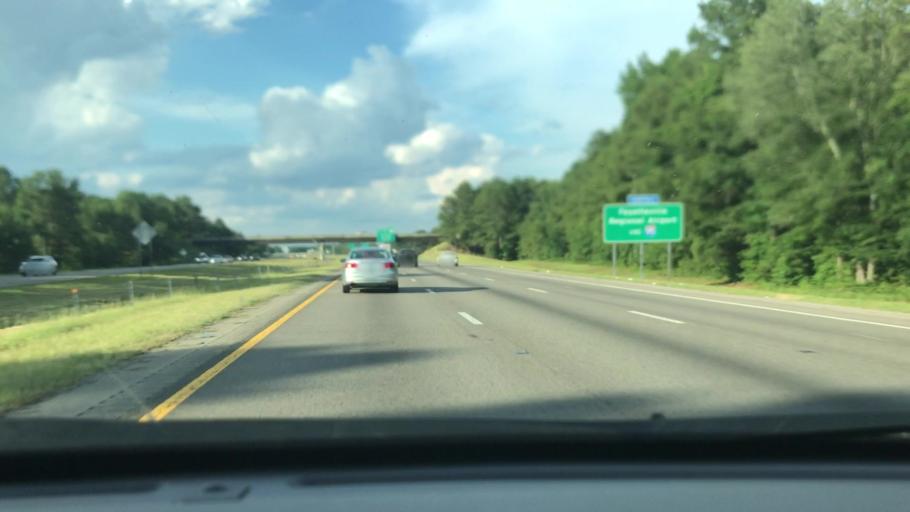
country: US
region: North Carolina
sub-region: Cumberland County
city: Hope Mills
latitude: 34.9193
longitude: -78.9484
